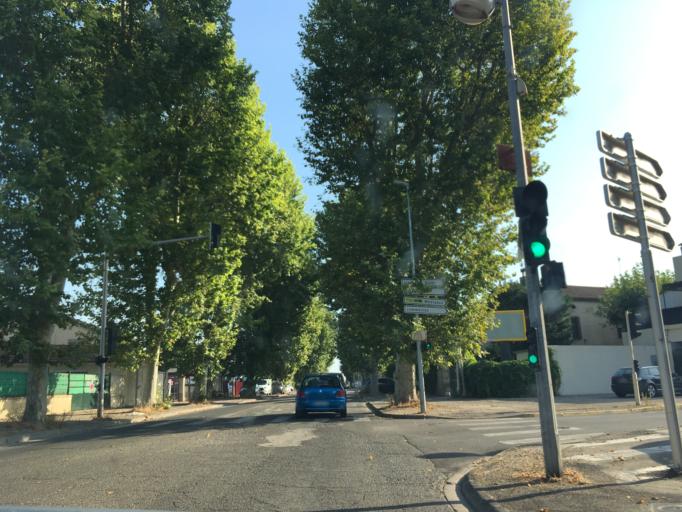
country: FR
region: Provence-Alpes-Cote d'Azur
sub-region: Departement des Bouches-du-Rhone
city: Arles
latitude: 43.6857
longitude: 4.6343
